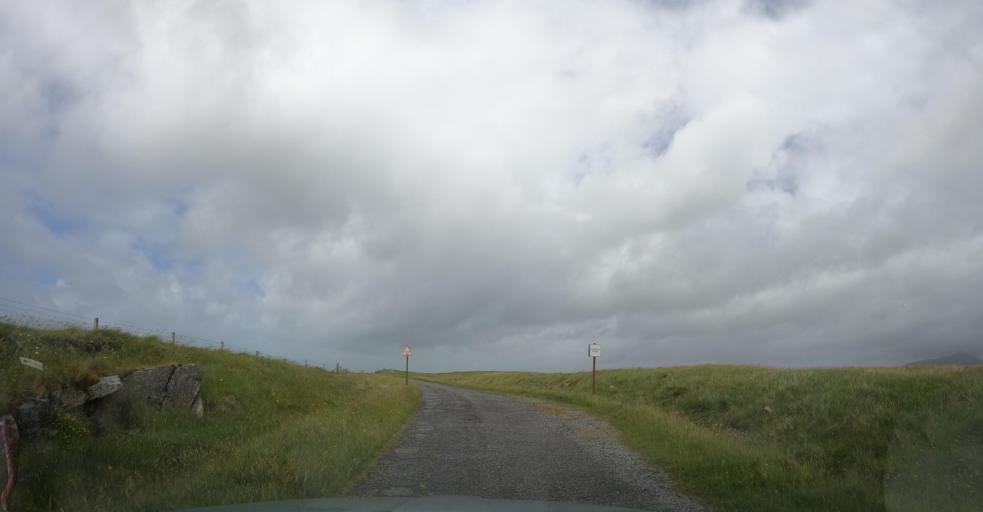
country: GB
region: Scotland
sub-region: Eilean Siar
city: Isle of South Uist
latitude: 57.2673
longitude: -7.3984
